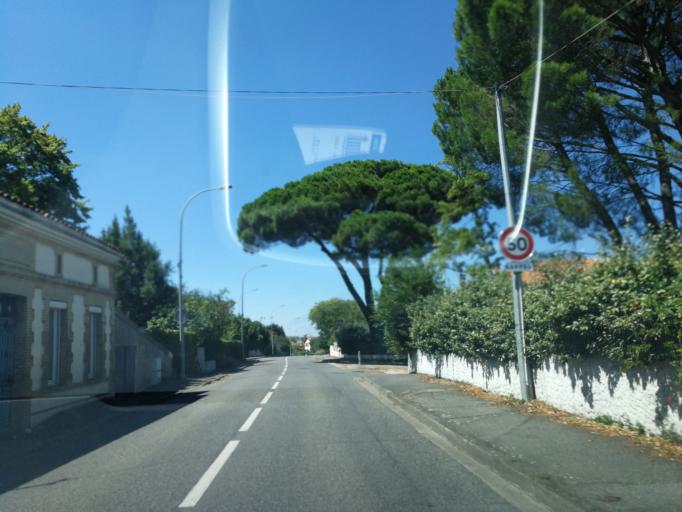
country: FR
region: Midi-Pyrenees
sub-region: Departement de la Haute-Garonne
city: Balma
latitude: 43.6094
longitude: 1.5061
